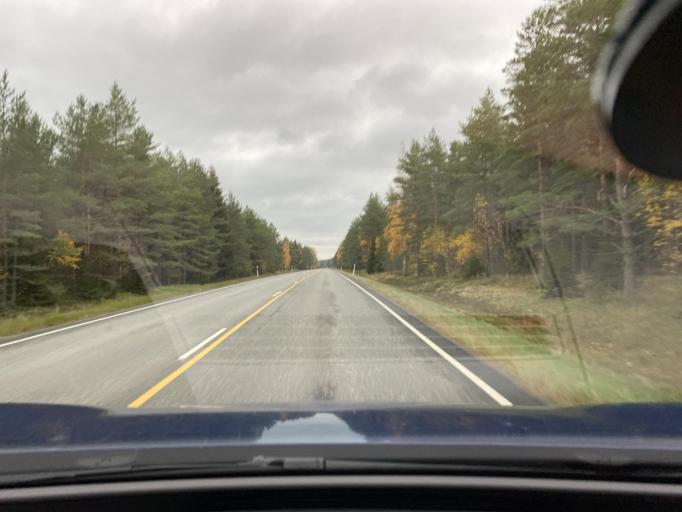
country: FI
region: Varsinais-Suomi
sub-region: Loimaa
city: Ylaene
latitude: 60.9080
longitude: 22.4105
